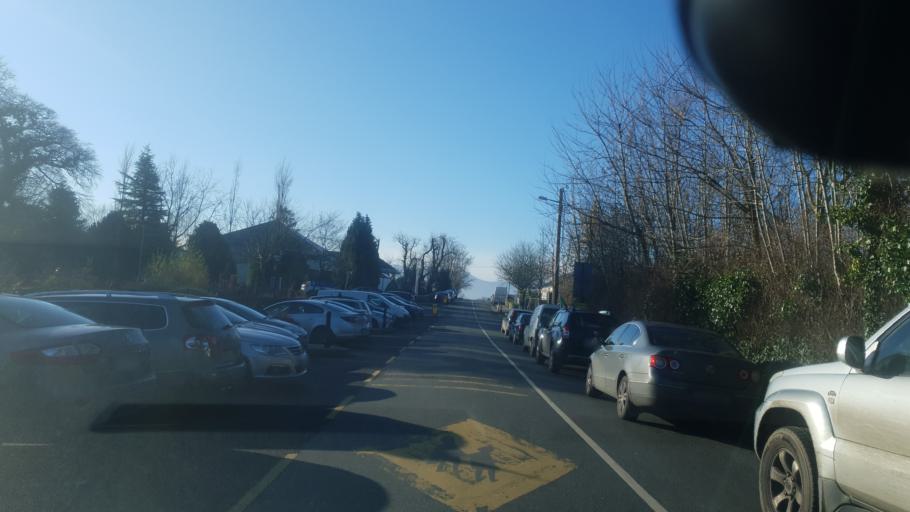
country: IE
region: Munster
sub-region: Ciarrai
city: Cill Airne
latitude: 52.0977
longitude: -9.4703
